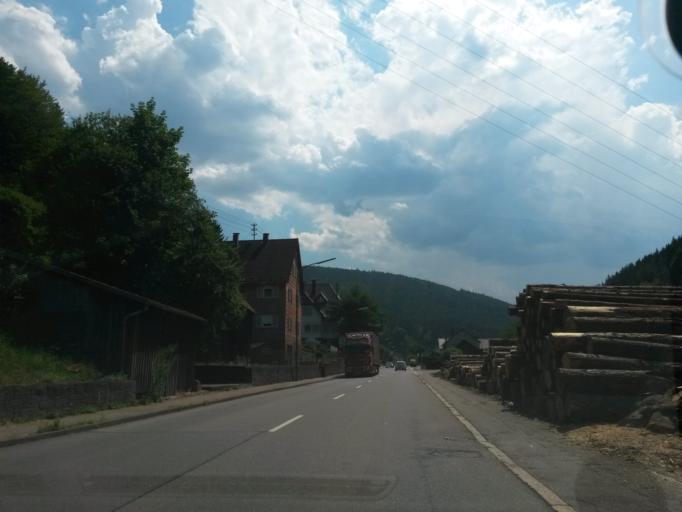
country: DE
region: Baden-Wuerttemberg
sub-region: Karlsruhe Region
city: Hofen an der Enz
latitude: 48.7679
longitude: 8.5866
